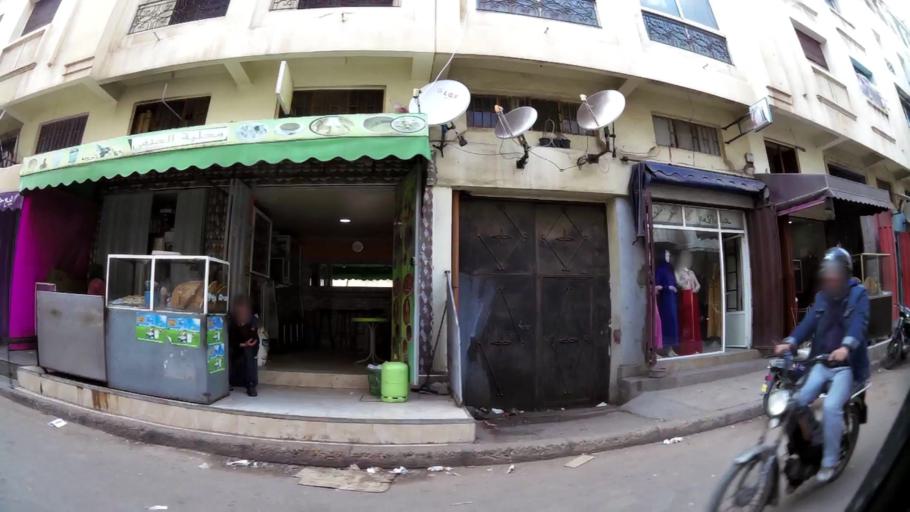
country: MA
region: Grand Casablanca
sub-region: Mohammedia
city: Mohammedia
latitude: 33.6850
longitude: -7.3787
